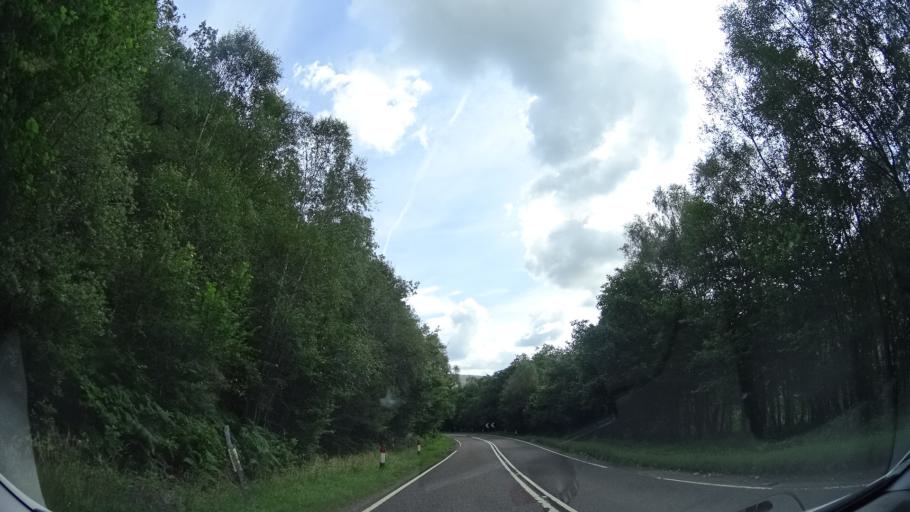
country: GB
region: Scotland
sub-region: Highland
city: Fort William
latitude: 56.8657
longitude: -5.4166
